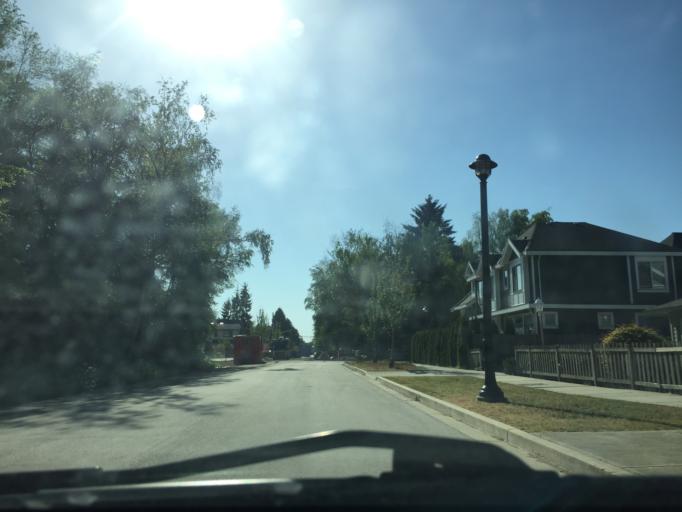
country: CA
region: British Columbia
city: Richmond
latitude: 49.1591
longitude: -123.1175
